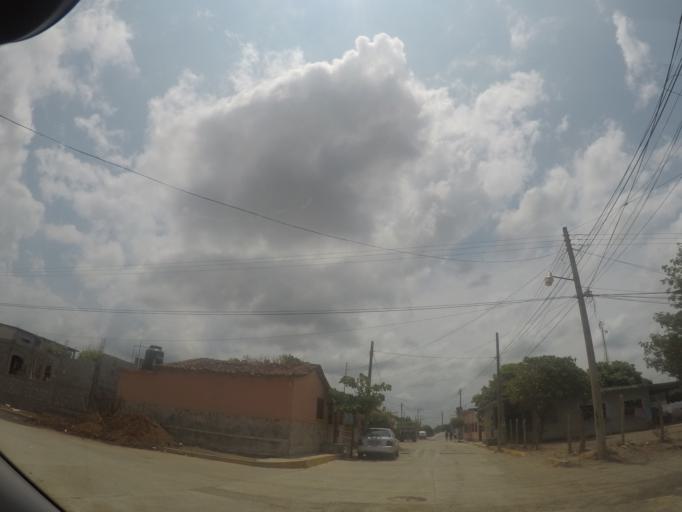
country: MX
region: Oaxaca
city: El Espinal
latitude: 16.5523
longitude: -94.9441
